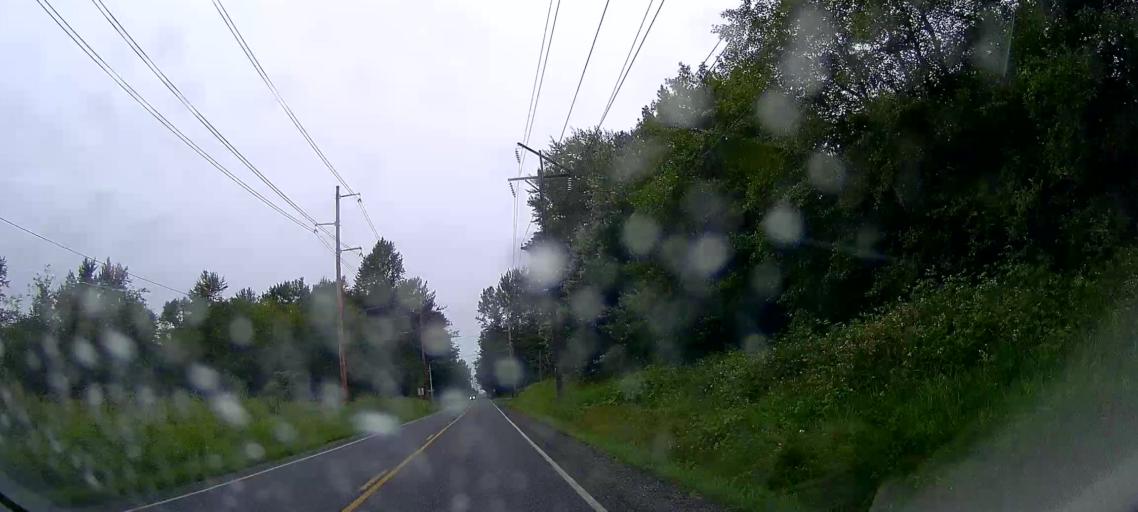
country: US
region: Washington
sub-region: Whatcom County
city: Birch Bay
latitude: 48.8765
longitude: -122.7042
